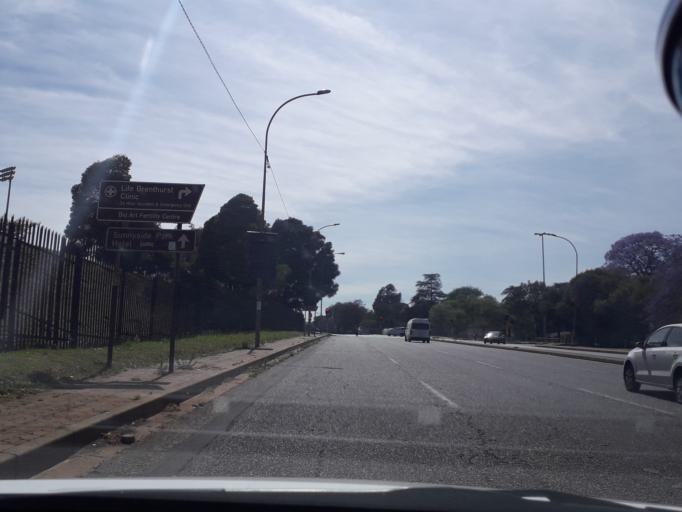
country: ZA
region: Gauteng
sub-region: City of Johannesburg Metropolitan Municipality
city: Johannesburg
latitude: -26.1817
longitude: 28.0413
